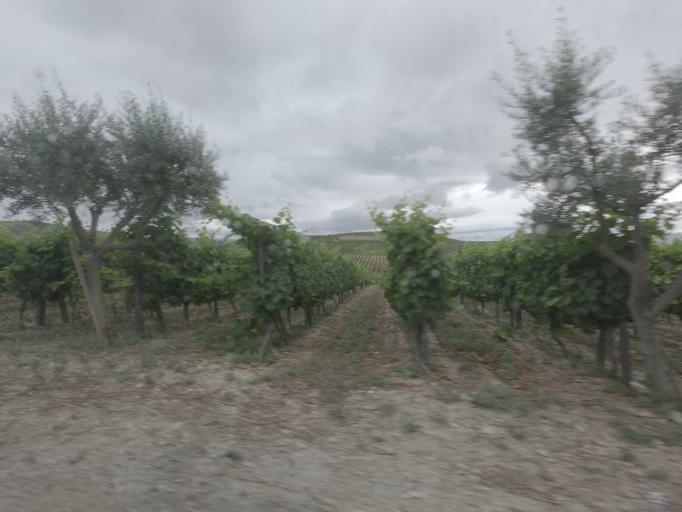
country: PT
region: Vila Real
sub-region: Sabrosa
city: Sabrosa
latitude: 41.2434
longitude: -7.4981
